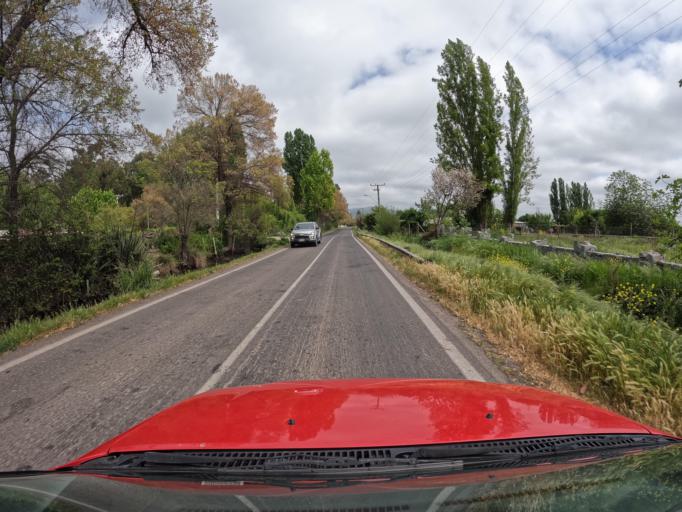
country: CL
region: O'Higgins
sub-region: Provincia de Colchagua
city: Santa Cruz
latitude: -34.6732
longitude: -71.3762
